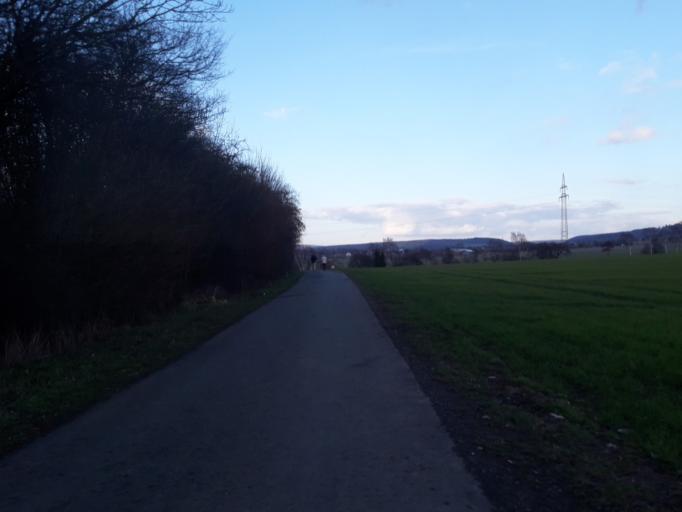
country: DE
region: North Rhine-Westphalia
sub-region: Regierungsbezirk Detmold
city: Paderborn
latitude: 51.7272
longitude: 8.8062
